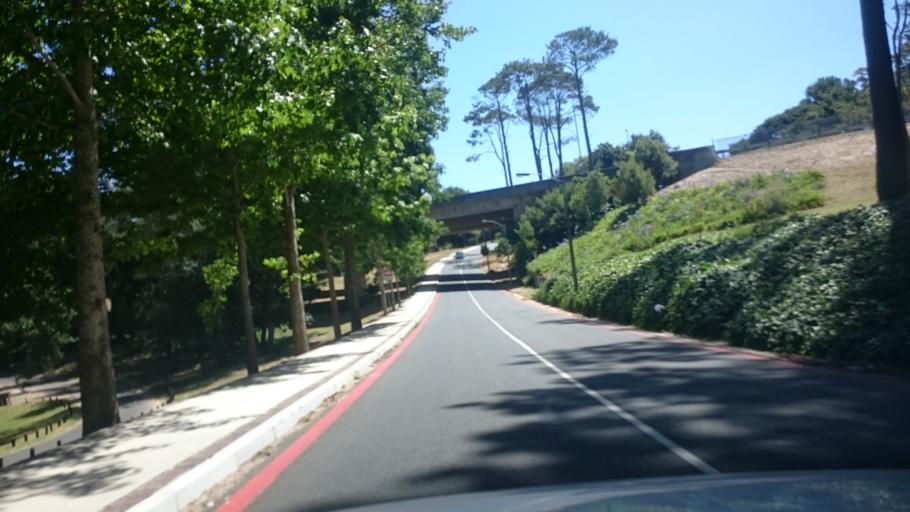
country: ZA
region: Western Cape
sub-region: City of Cape Town
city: Newlands
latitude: -33.9997
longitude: 18.4510
